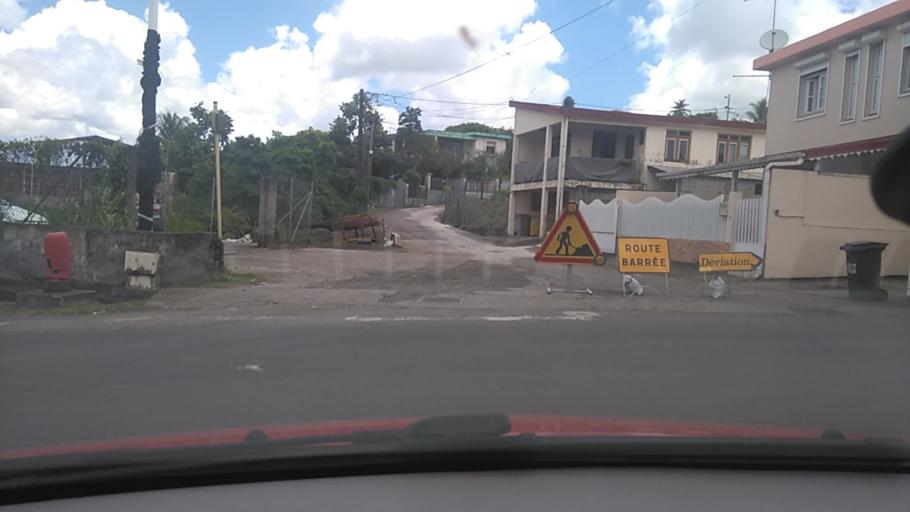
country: MQ
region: Martinique
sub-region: Martinique
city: Saint-Esprit
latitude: 14.5627
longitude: -60.9382
